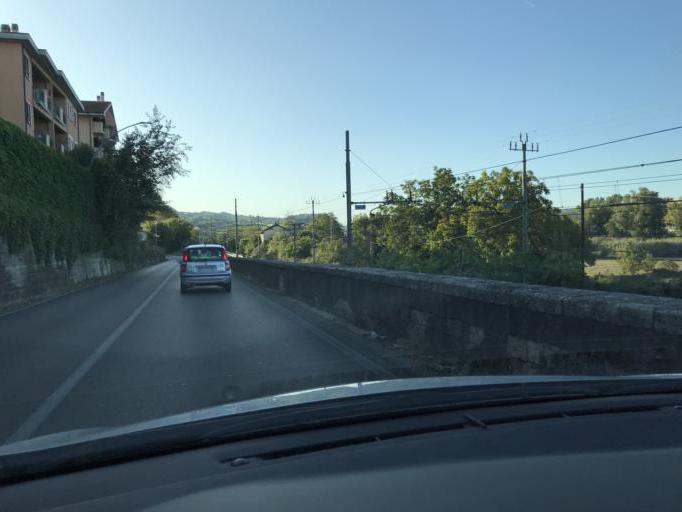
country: IT
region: Latium
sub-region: Provincia di Viterbo
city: Orte Scalo
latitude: 42.4432
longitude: 12.4043
